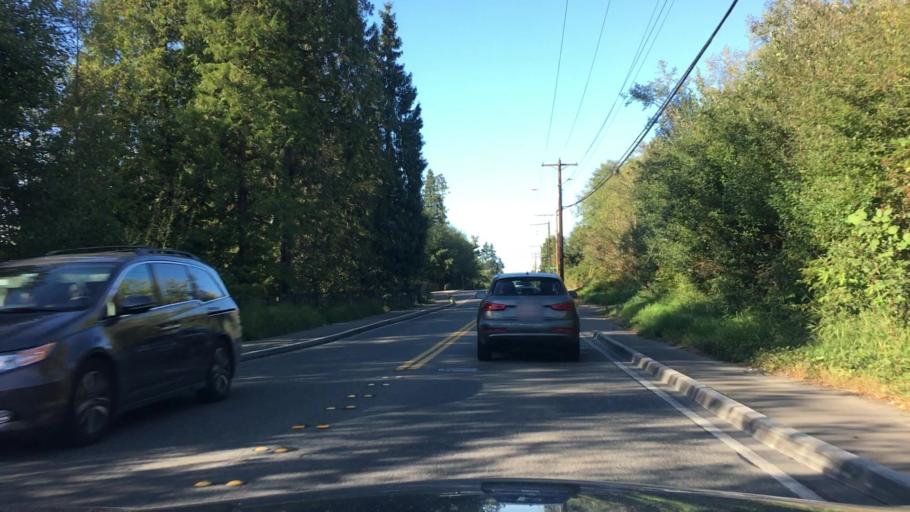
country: US
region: Washington
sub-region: Snohomish County
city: North Creek
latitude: 47.7919
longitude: -122.1812
